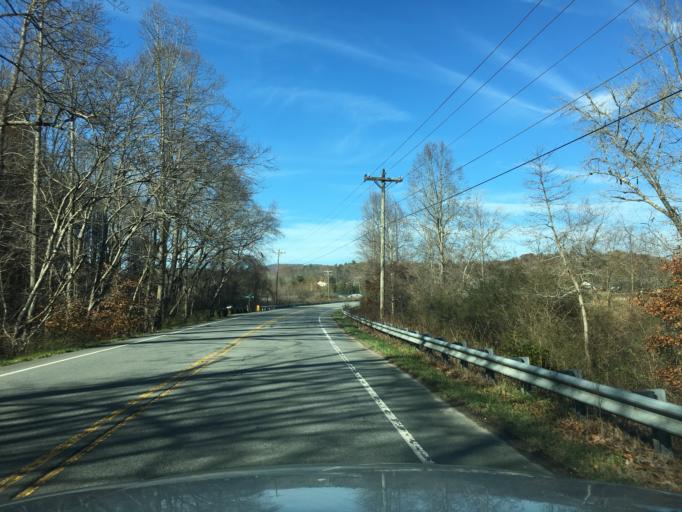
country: US
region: North Carolina
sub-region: Henderson County
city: Etowah
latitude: 35.2958
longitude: -82.6265
